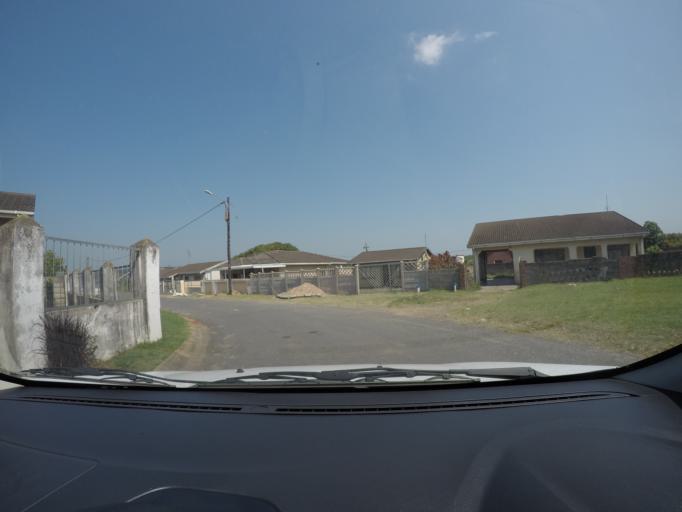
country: ZA
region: KwaZulu-Natal
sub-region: uThungulu District Municipality
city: eSikhawini
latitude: -28.8676
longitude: 31.9172
